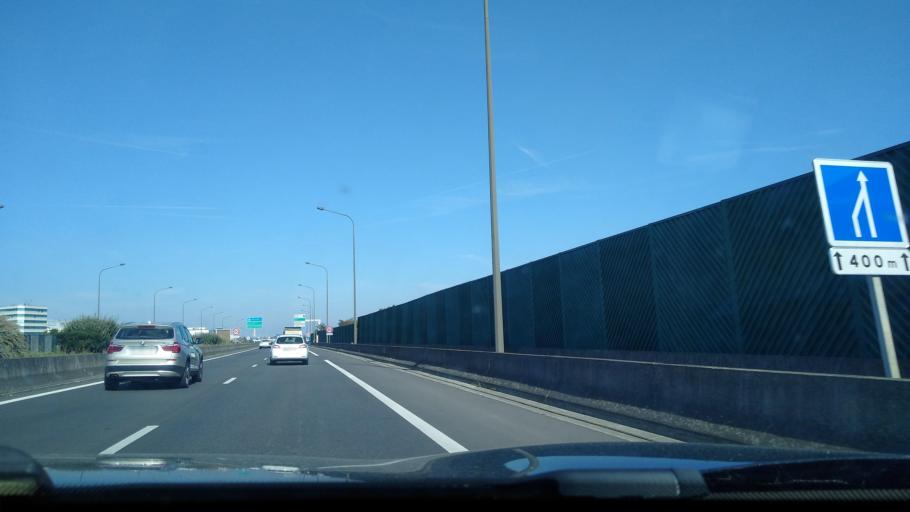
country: FR
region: Midi-Pyrenees
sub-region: Departement de la Haute-Garonne
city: Colomiers
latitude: 43.6035
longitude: 1.3671
